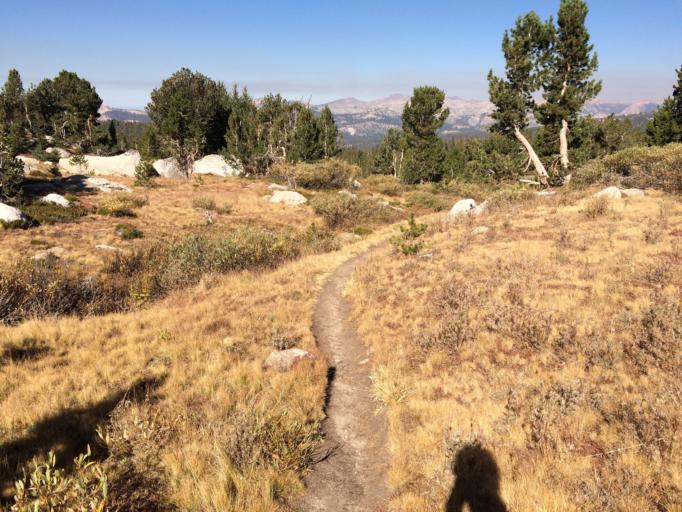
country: US
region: California
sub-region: Mariposa County
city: Yosemite Valley
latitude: 37.9379
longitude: -119.3359
